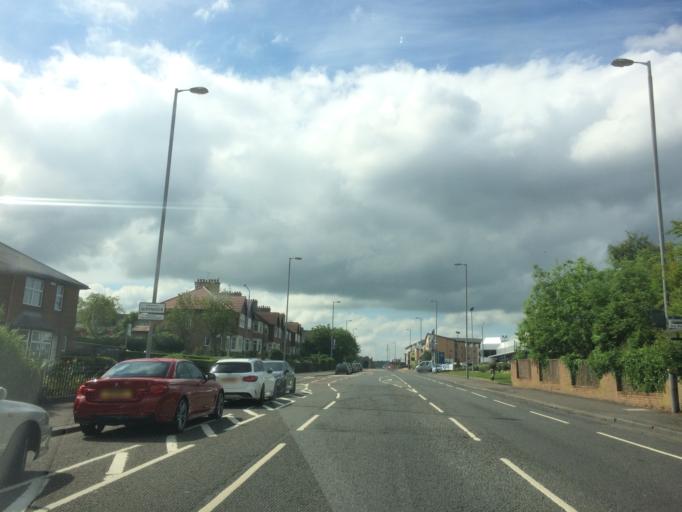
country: GB
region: Scotland
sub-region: East Renfrewshire
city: Giffnock
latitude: 55.8098
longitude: -4.2937
